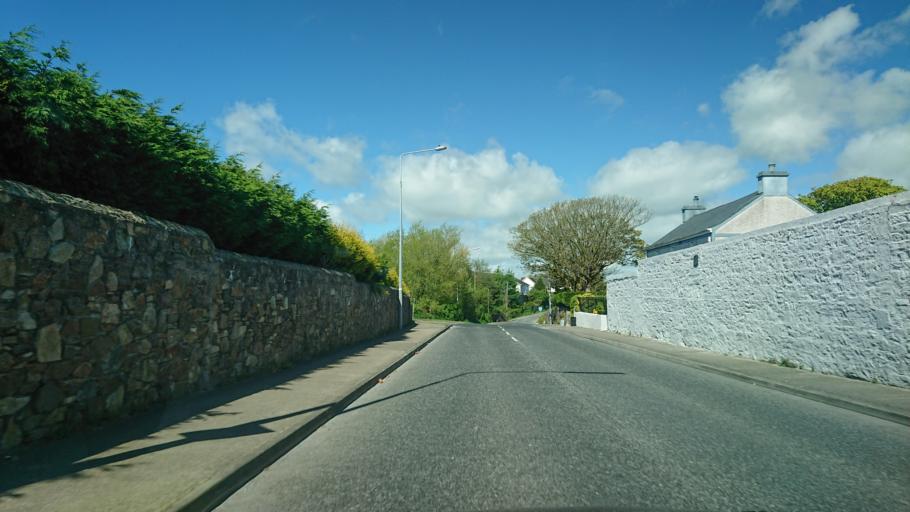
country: IE
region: Munster
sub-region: Waterford
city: Waterford
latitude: 52.2648
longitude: -7.1349
